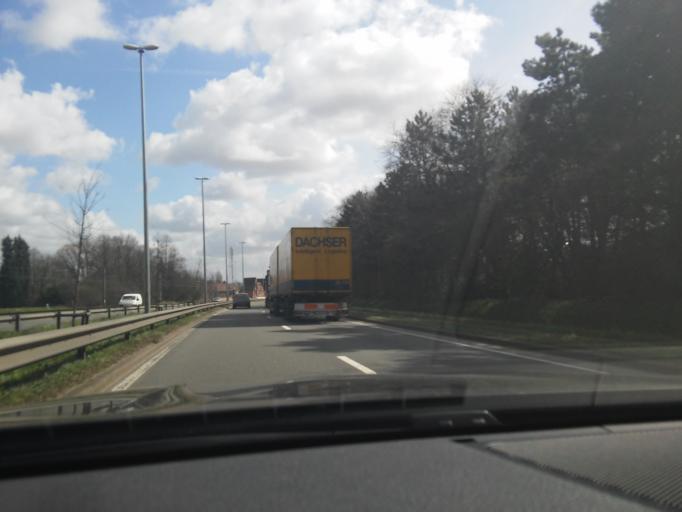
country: BE
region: Flanders
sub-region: Provincie Oost-Vlaanderen
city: Temse
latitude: 51.1325
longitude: 4.2166
